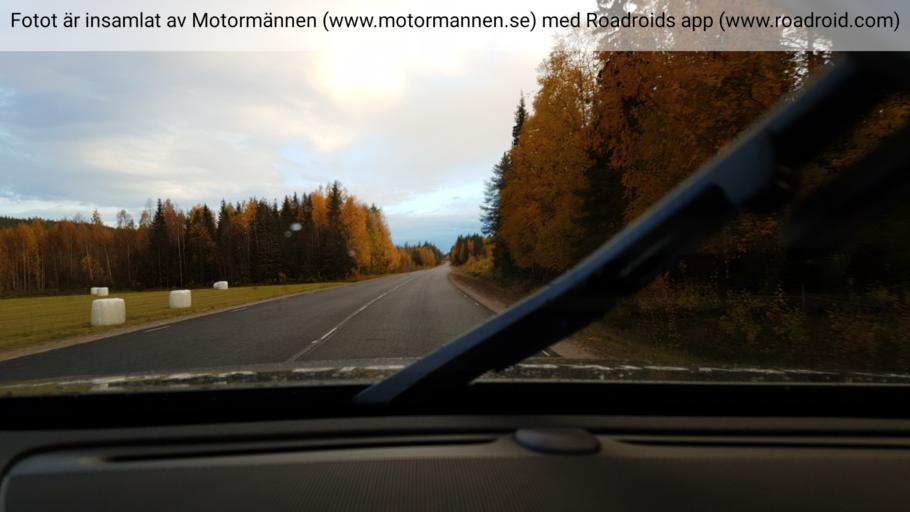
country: SE
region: Norrbotten
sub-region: Overkalix Kommun
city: OEverkalix
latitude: 66.4174
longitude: 22.8038
